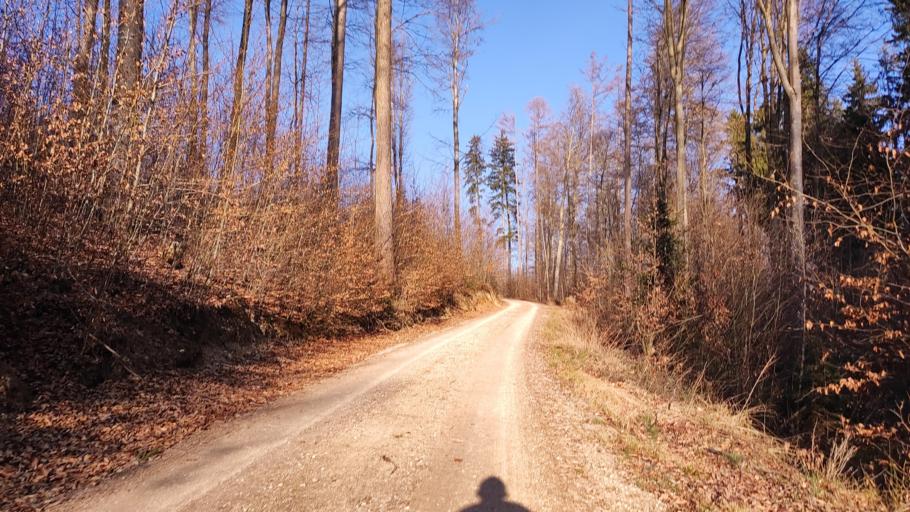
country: DE
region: Bavaria
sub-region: Swabia
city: Zusmarshausen
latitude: 48.4272
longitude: 10.6182
